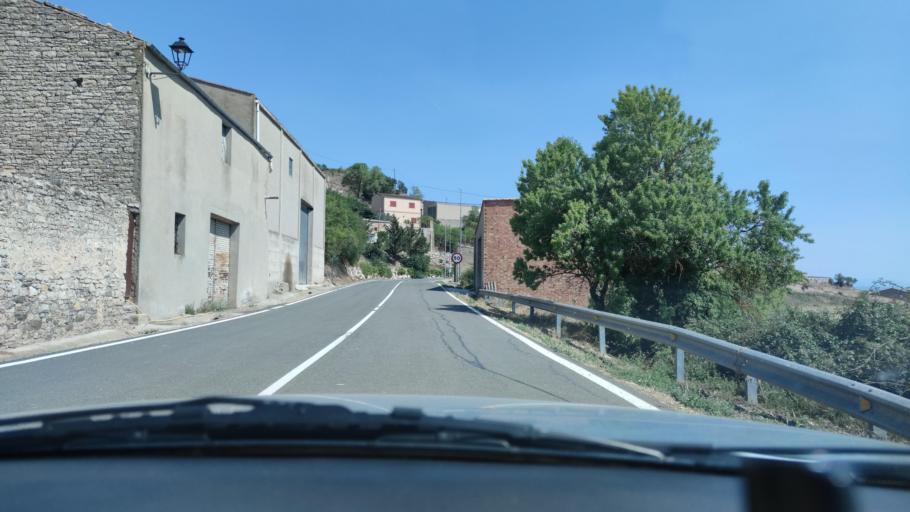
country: ES
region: Catalonia
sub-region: Provincia de Tarragona
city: Santa Coloma de Queralt
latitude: 41.5817
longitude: 1.3391
